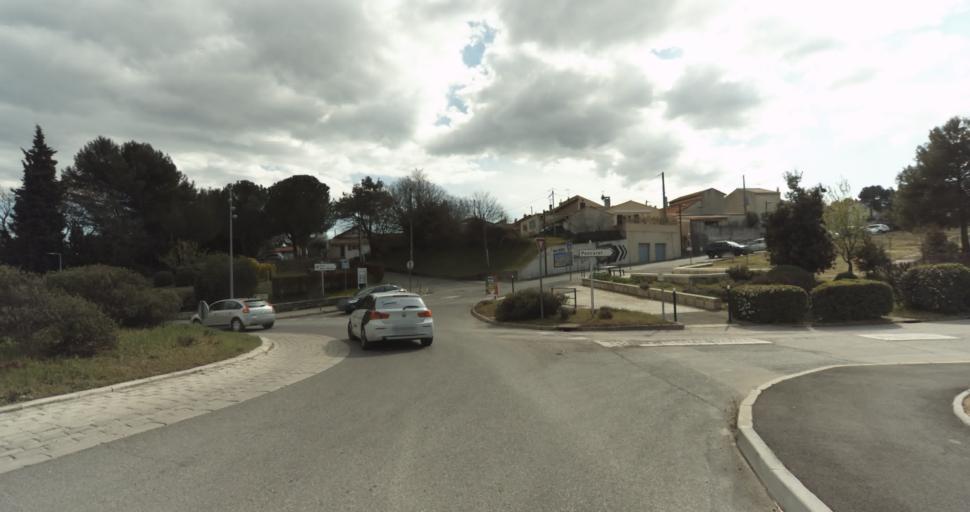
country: FR
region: Provence-Alpes-Cote d'Azur
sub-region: Departement des Bouches-du-Rhone
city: Greasque
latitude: 43.4349
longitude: 5.5384
